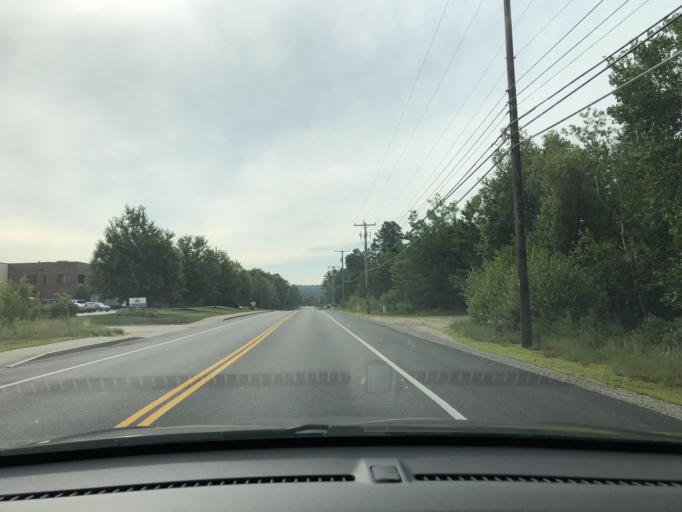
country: US
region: New Hampshire
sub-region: Merrimack County
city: Concord
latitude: 43.2110
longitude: -71.4933
